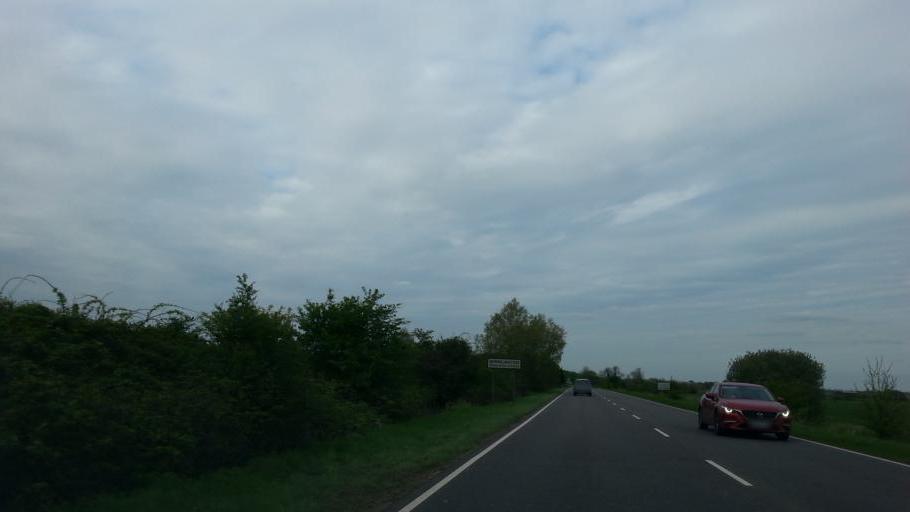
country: GB
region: England
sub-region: Cambridgeshire
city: Doddington
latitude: 52.5000
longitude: 0.0788
